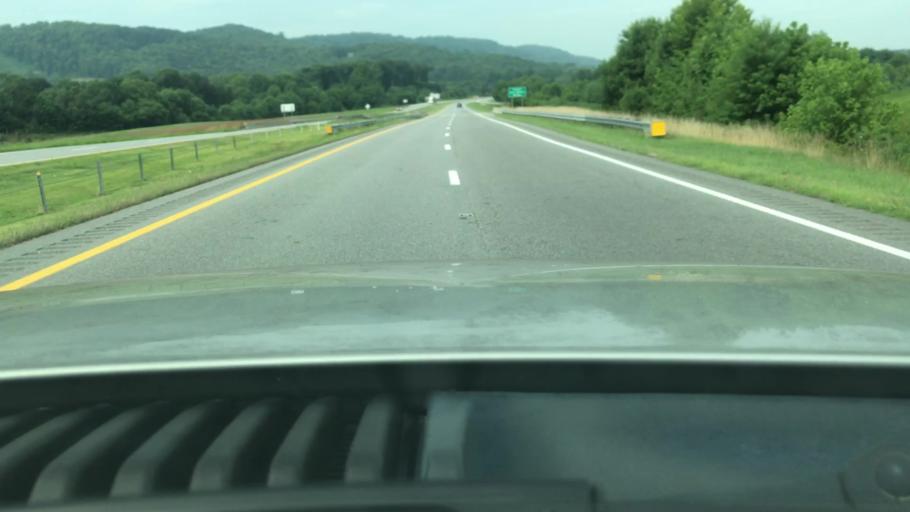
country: US
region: North Carolina
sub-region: Wilkes County
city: North Wilkesboro
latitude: 36.1547
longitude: -80.9923
